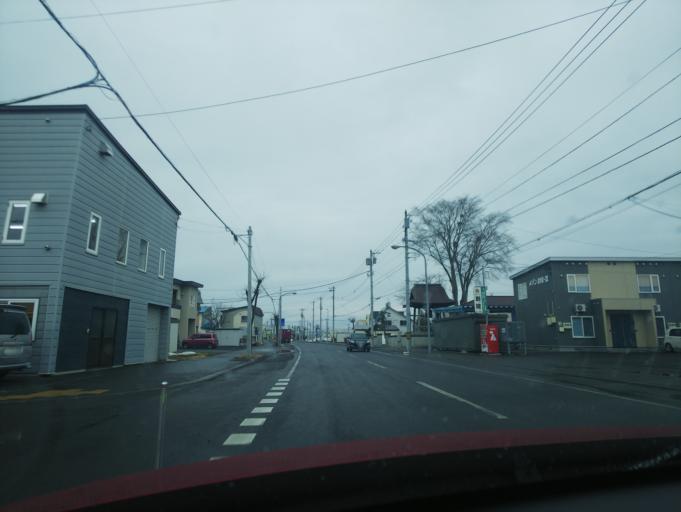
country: JP
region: Hokkaido
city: Nayoro
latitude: 44.3446
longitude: 142.4642
